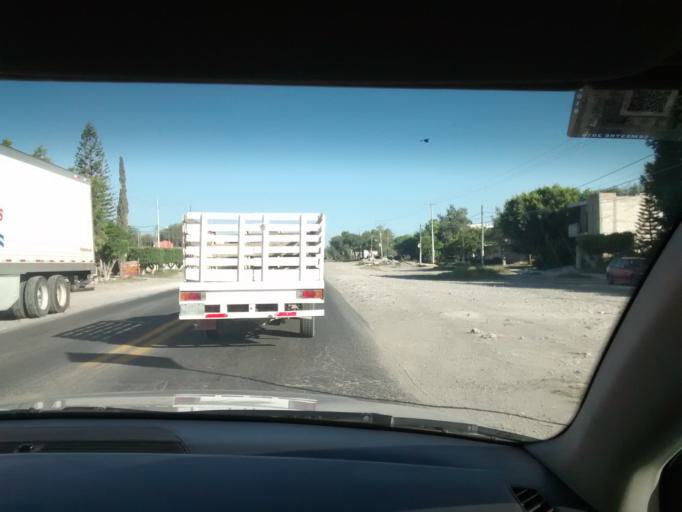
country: MX
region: Puebla
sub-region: Tehuacan
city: Magdalena Cuayucatepec
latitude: 18.5130
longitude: -97.4953
